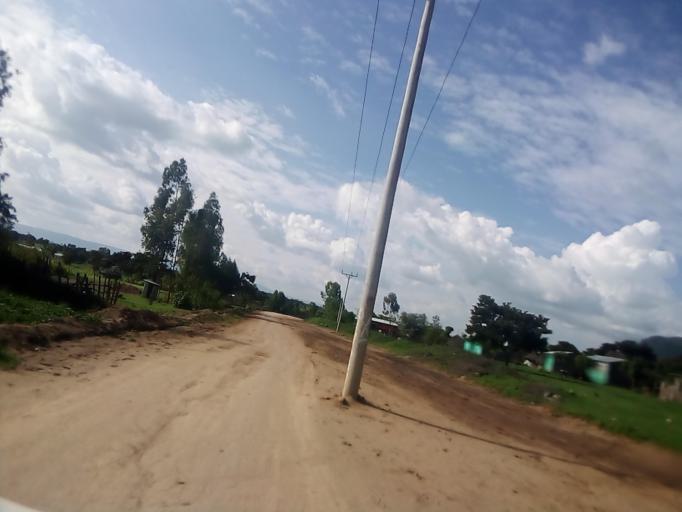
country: ET
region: Southern Nations, Nationalities, and People's Region
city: K'olito
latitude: 7.6149
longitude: 38.0649
